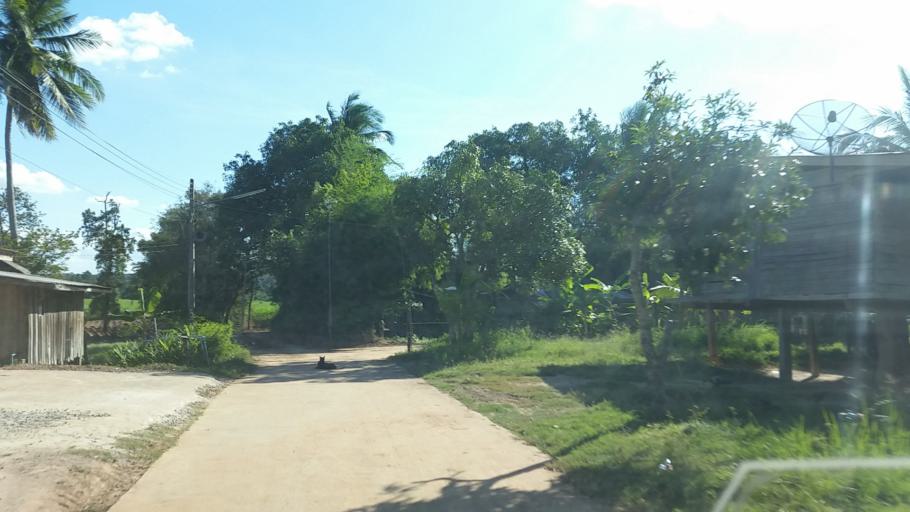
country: TH
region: Chaiyaphum
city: Thep Sathit
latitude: 15.5399
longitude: 101.4884
